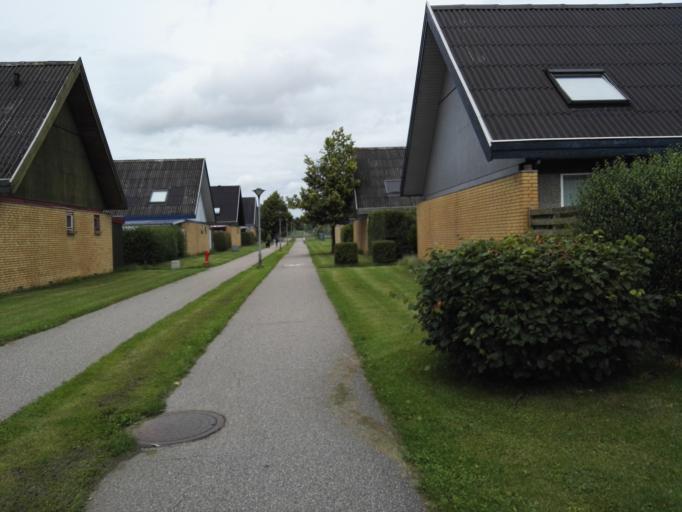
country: DK
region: Capital Region
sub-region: Egedal Kommune
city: Stenlose
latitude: 55.7759
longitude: 12.1780
